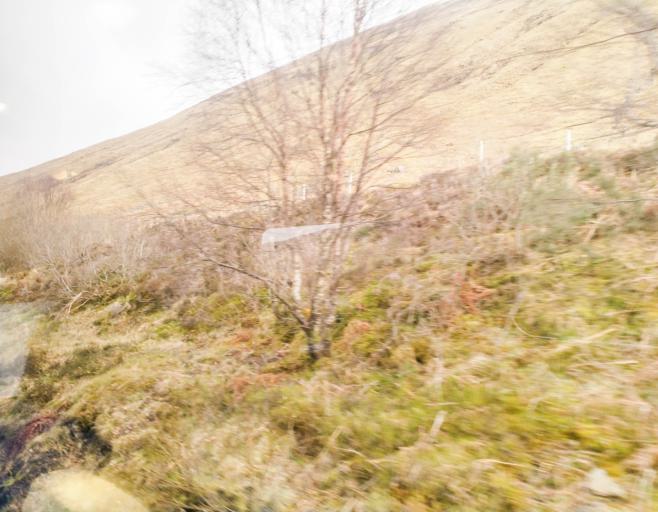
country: GB
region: Scotland
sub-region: Argyll and Bute
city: Garelochhead
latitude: 56.4648
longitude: -4.7154
